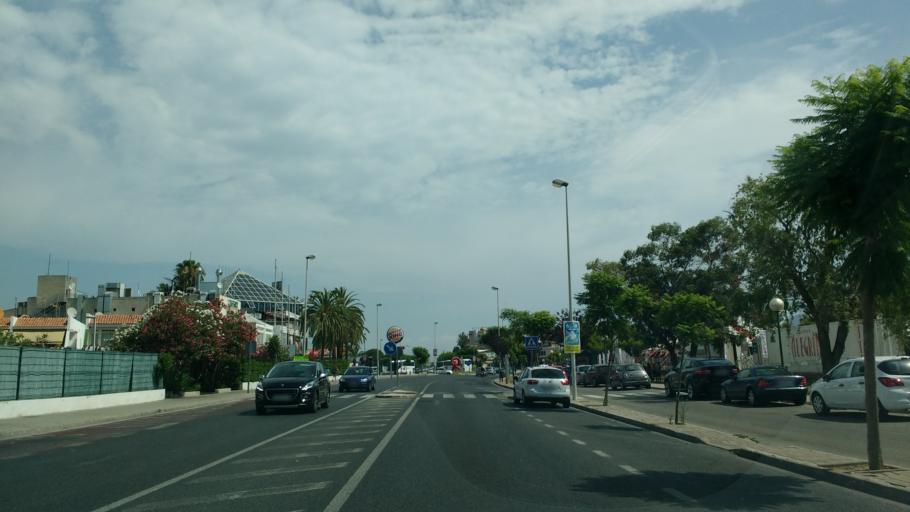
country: ES
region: Balearic Islands
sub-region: Illes Balears
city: Port d'Alcudia
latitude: 39.8385
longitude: 3.1202
